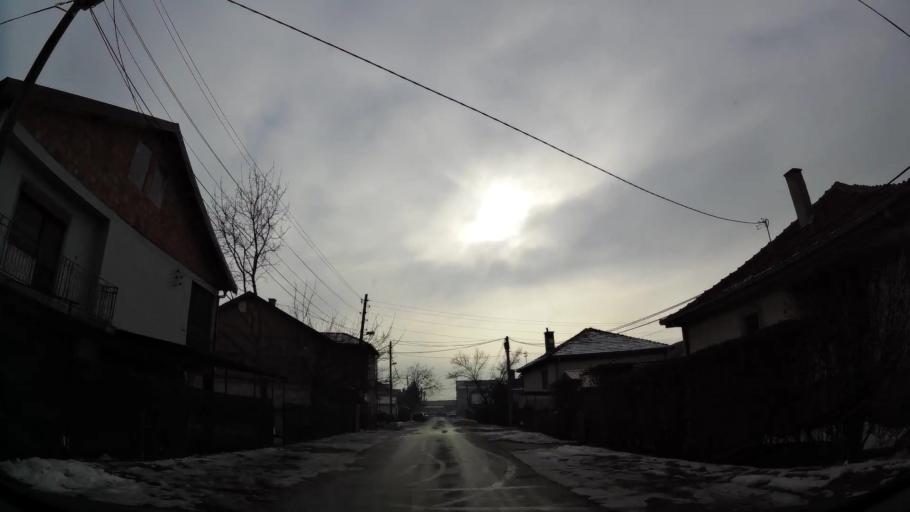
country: MK
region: Ilinden
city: Ilinden
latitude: 41.9925
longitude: 21.5843
